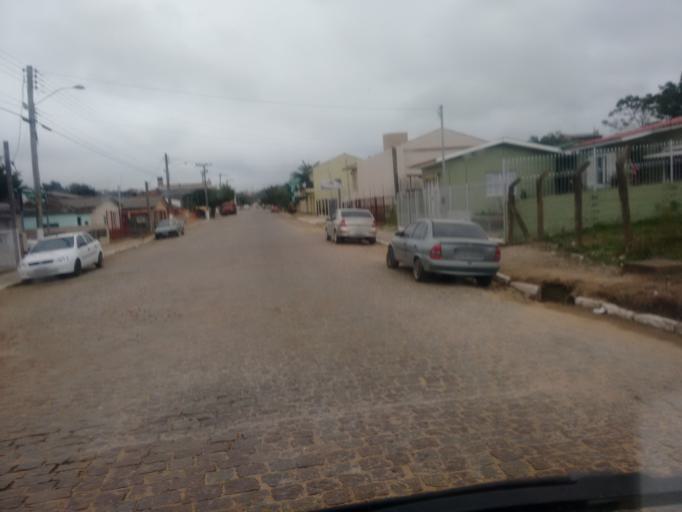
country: BR
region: Rio Grande do Sul
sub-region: Camaqua
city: Camaqua
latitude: -30.8416
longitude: -51.8151
